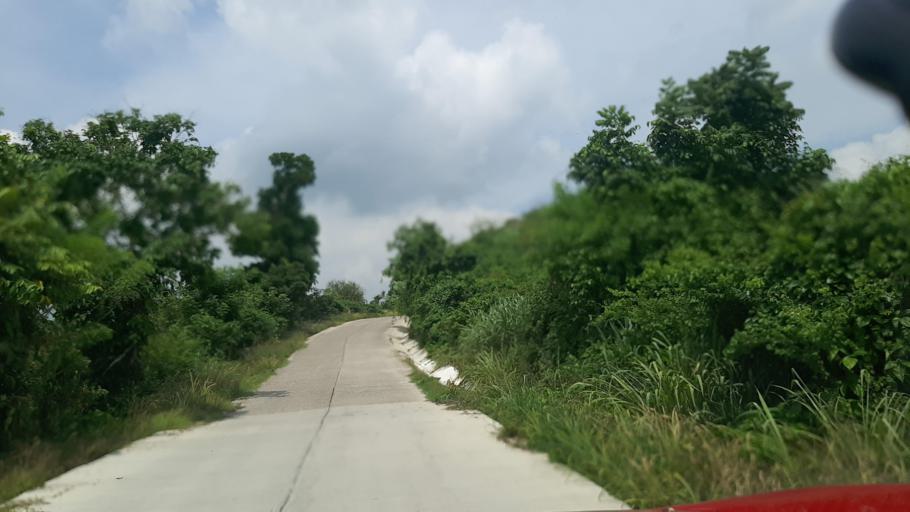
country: MX
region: Veracruz
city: Gutierrez Zamora
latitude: 20.4445
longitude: -97.1702
